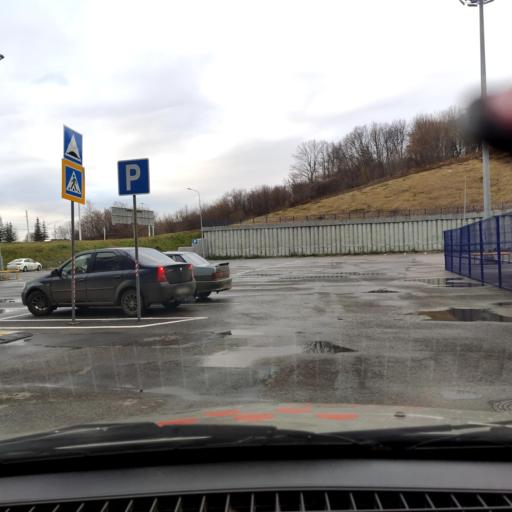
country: RU
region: Bashkortostan
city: Ufa
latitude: 54.7640
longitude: 56.0415
